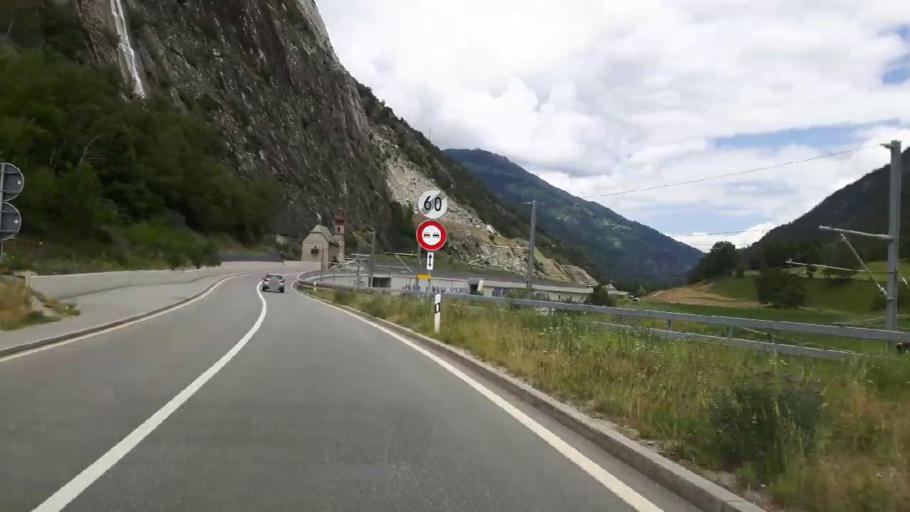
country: CH
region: Valais
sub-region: Brig District
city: Naters
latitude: 46.3426
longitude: 8.0255
